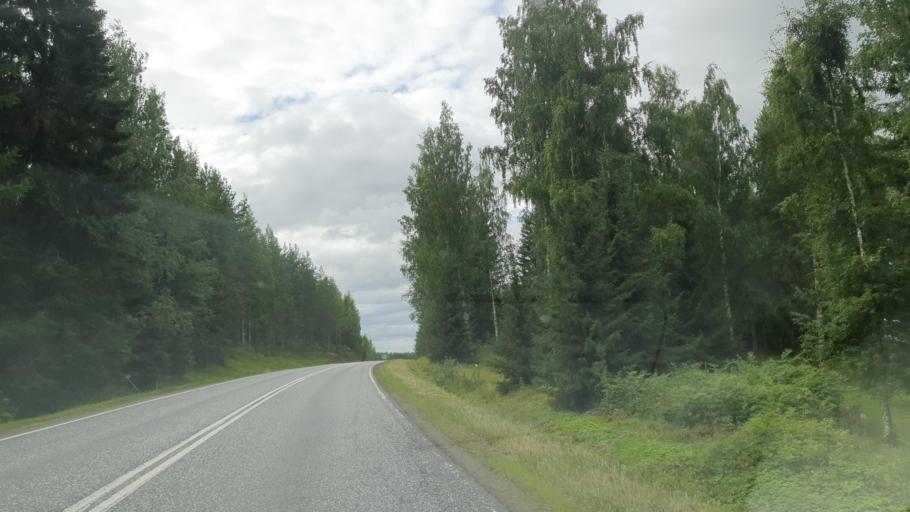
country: FI
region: Northern Savo
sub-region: Ylae-Savo
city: Iisalmi
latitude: 63.5194
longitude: 27.2008
